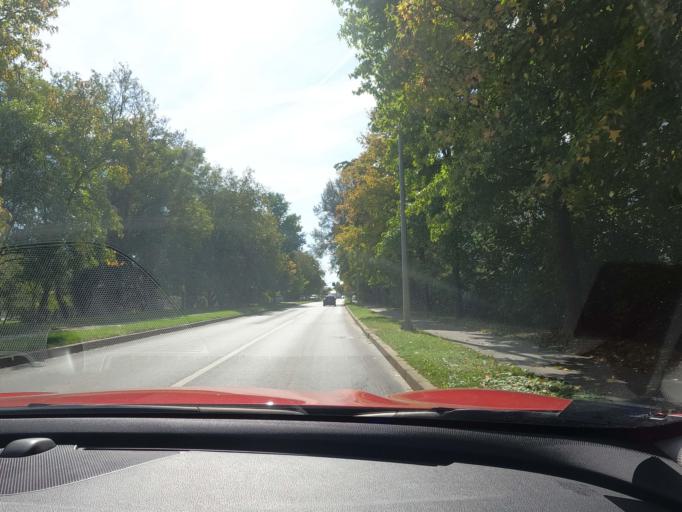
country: HR
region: Sisacko-Moslavacka
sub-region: Grad Sisak
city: Sisak
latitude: 45.4941
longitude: 16.3812
